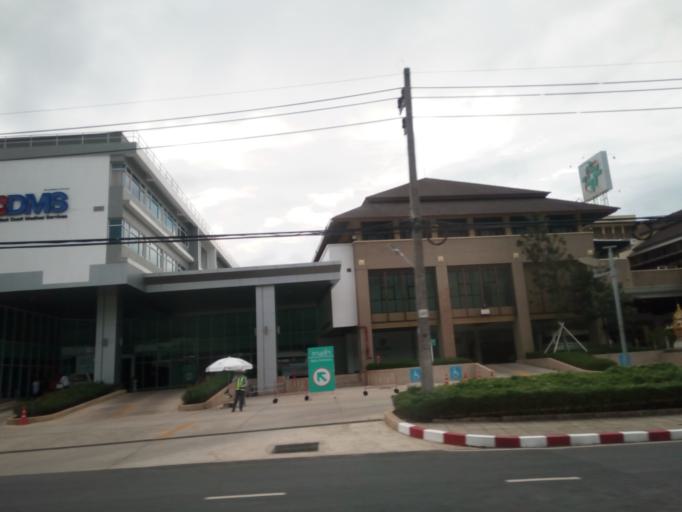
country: TH
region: Phuket
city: Wichit
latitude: 7.8960
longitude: 98.3682
